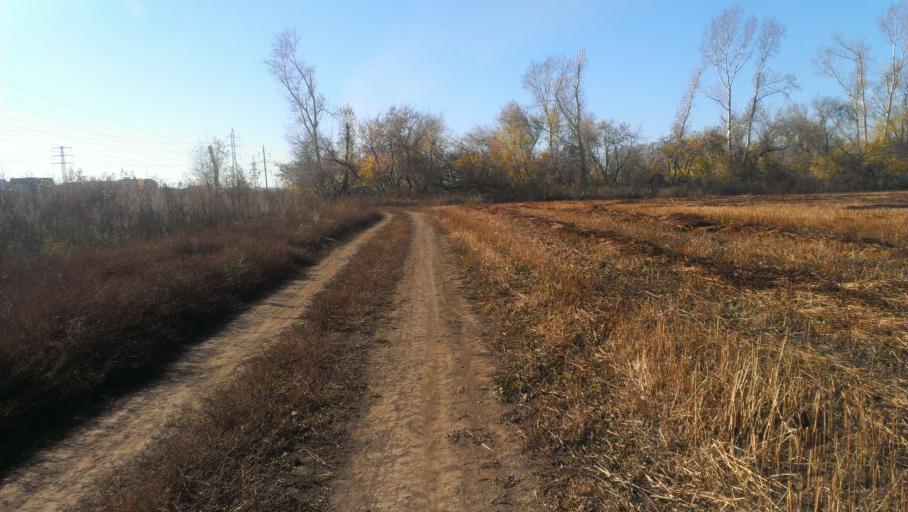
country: RU
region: Altai Krai
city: Novosilikatnyy
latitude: 53.3632
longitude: 83.6381
